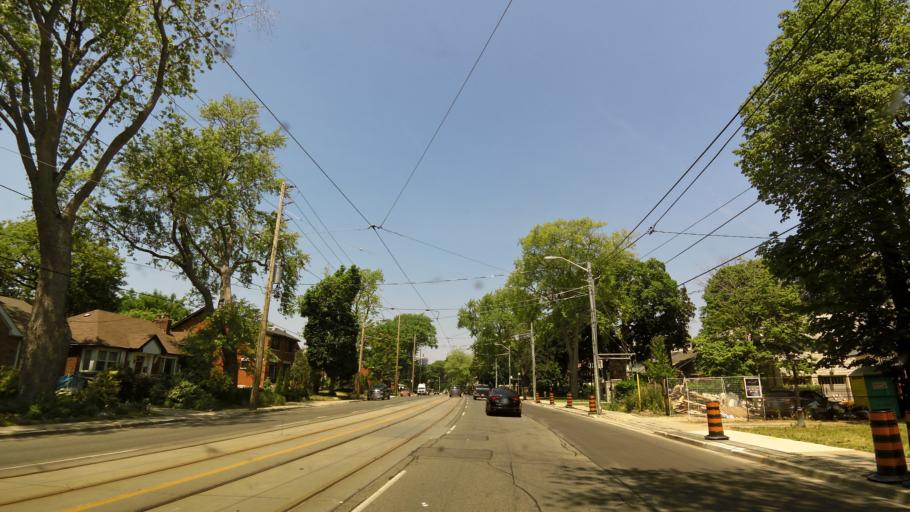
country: CA
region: Ontario
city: Etobicoke
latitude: 43.6050
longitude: -79.4913
